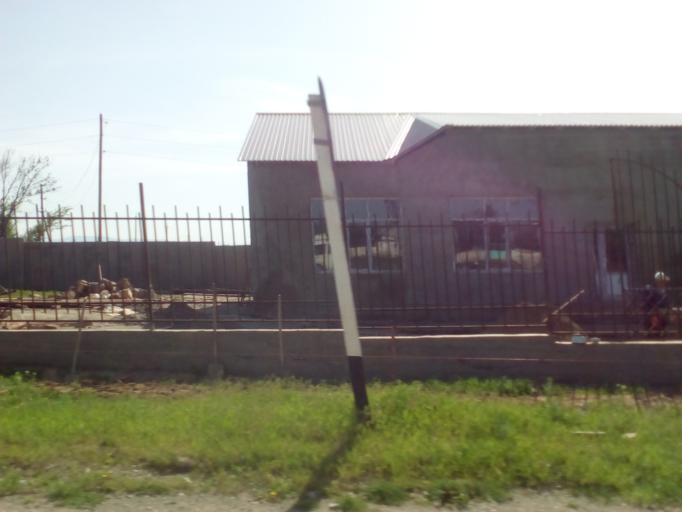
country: KZ
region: Ongtustik Qazaqstan
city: Shayan
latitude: 43.0477
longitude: 69.3899
